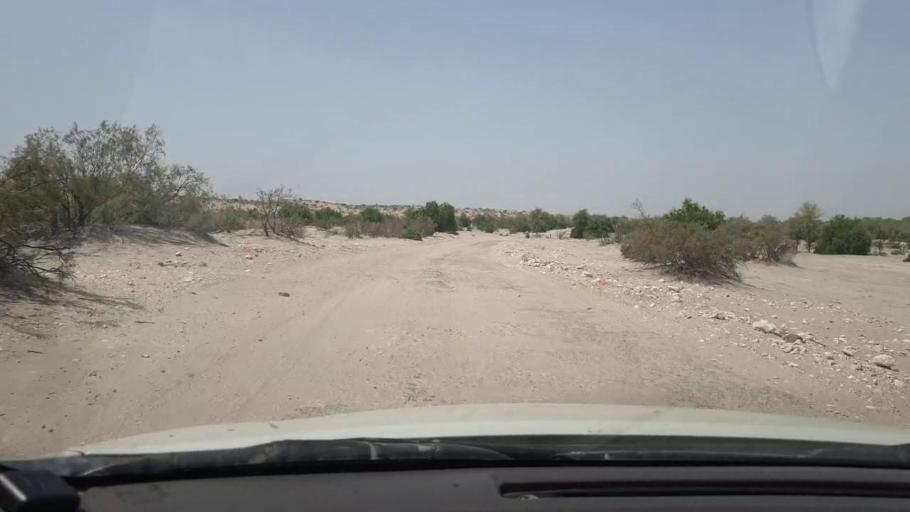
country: PK
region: Sindh
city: Rohri
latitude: 27.3037
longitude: 69.2810
